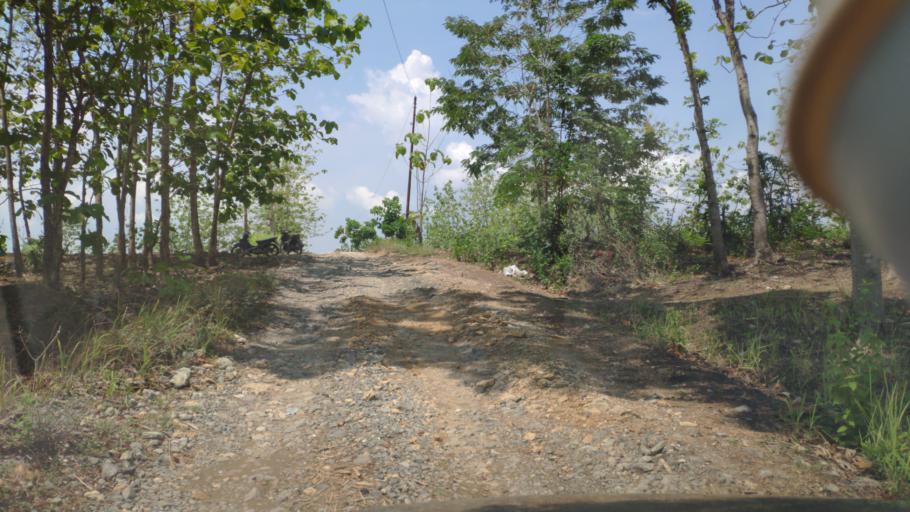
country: ID
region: Central Java
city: Balong Wetan
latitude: -7.0062
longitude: 111.2540
